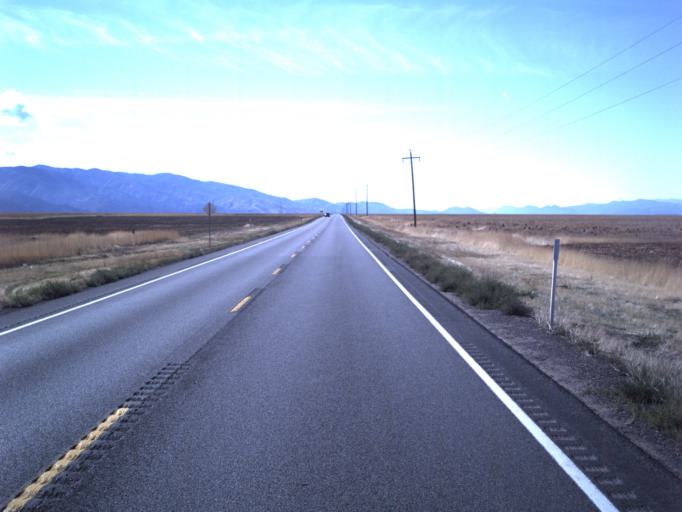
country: US
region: Utah
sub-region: Juab County
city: Nephi
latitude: 39.6430
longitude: -111.8615
